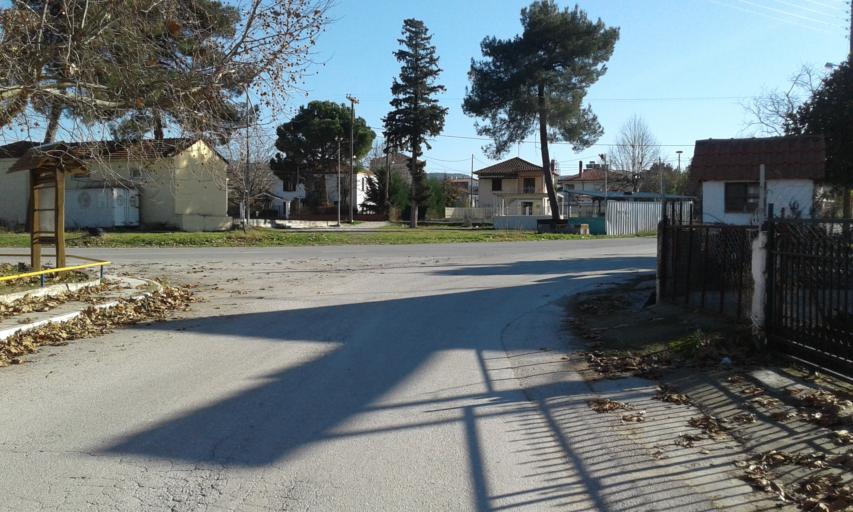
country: GR
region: Central Macedonia
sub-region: Nomos Thessalonikis
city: Gerakarou
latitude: 40.6368
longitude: 23.2450
